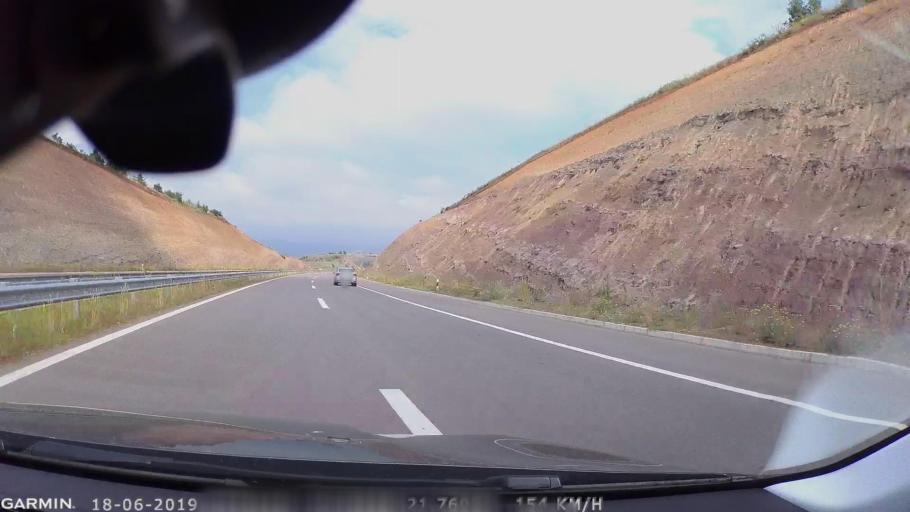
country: MK
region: Sveti Nikole
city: Gorobinci
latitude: 41.9245
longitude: 21.8415
